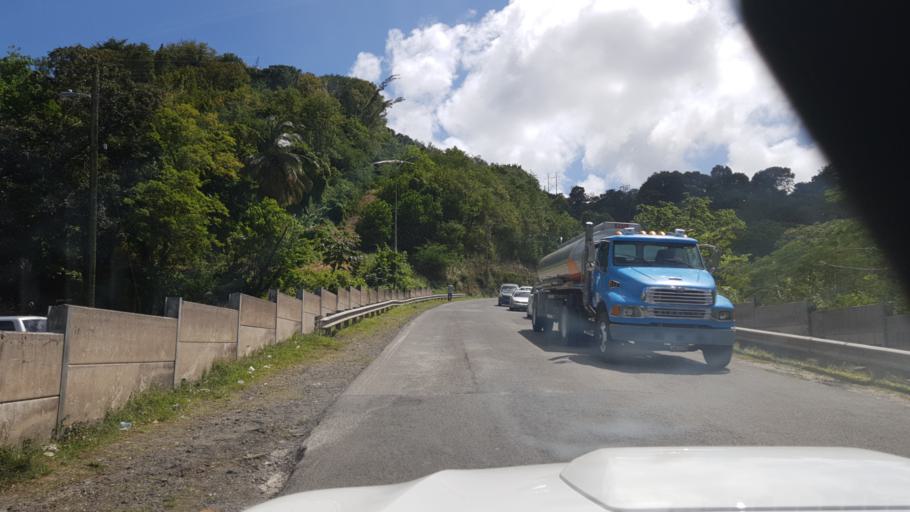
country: LC
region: Castries Quarter
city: Castries
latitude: 14.0092
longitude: -60.9996
